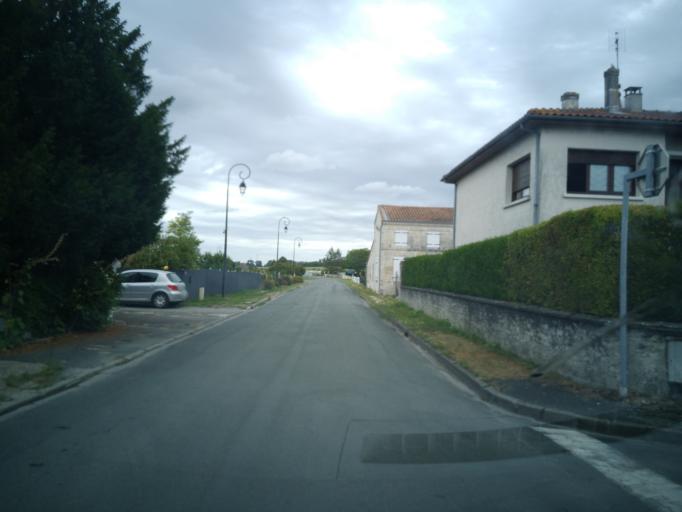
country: FR
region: Poitou-Charentes
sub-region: Departement de la Charente-Maritime
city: Pons
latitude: 45.5988
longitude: -0.5137
